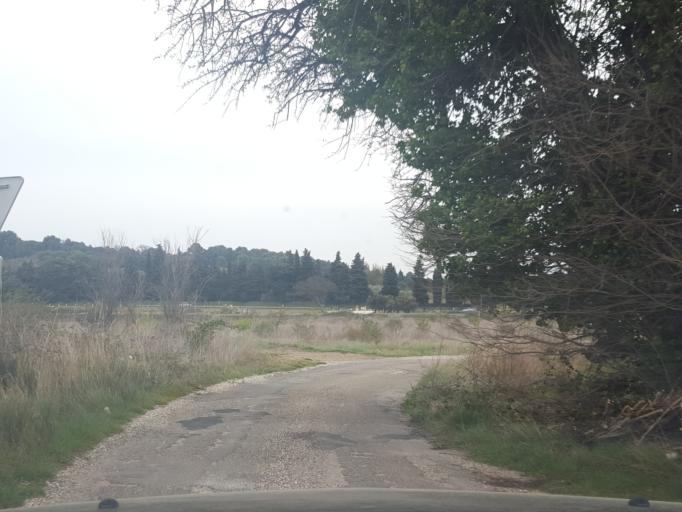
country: FR
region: Provence-Alpes-Cote d'Azur
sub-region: Departement du Vaucluse
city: Saint-Saturnin-les-Avignon
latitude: 43.9526
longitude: 4.9134
